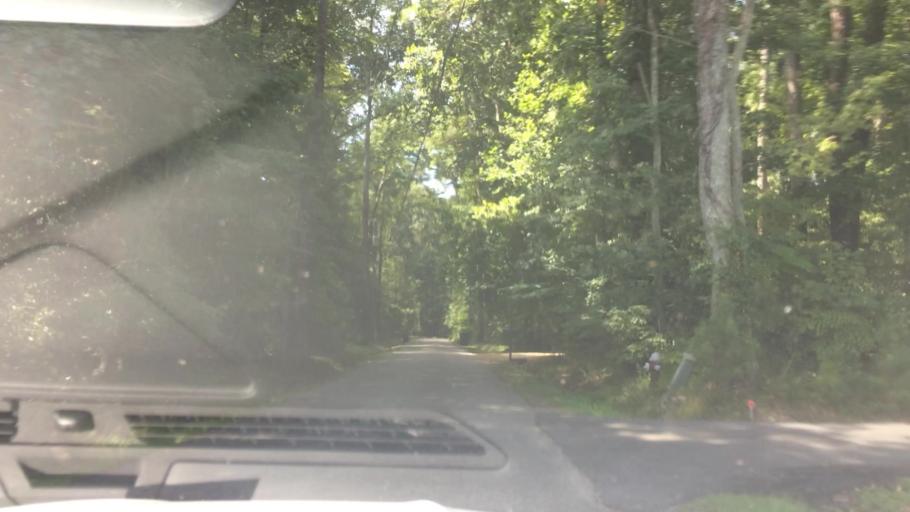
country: US
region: Virginia
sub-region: City of Poquoson
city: Poquoson
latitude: 37.1611
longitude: -76.4265
